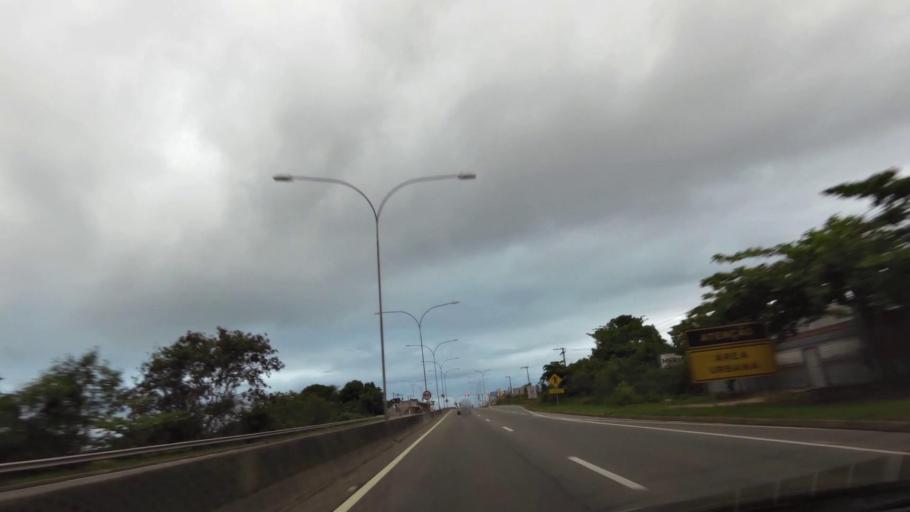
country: BR
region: Espirito Santo
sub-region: Viana
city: Viana
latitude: -20.5046
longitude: -40.3643
